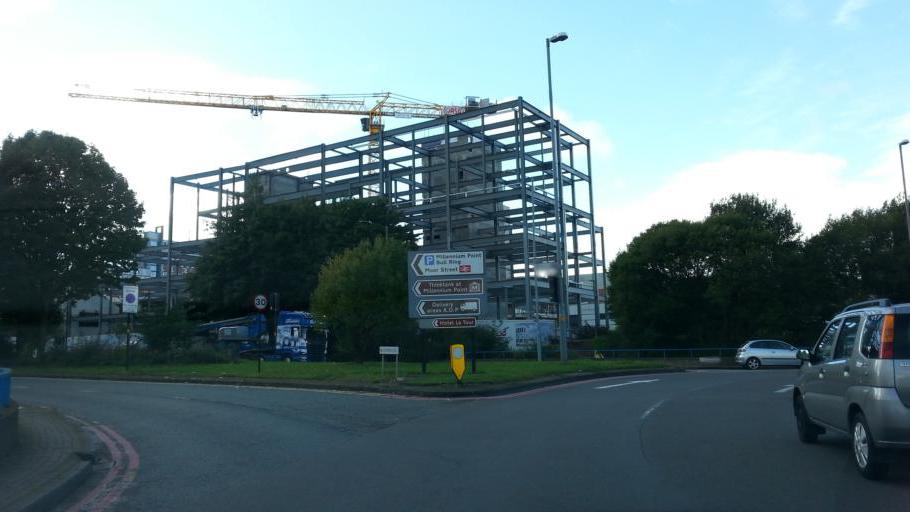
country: GB
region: England
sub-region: City and Borough of Birmingham
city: Birmingham
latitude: 52.4859
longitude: -1.8829
